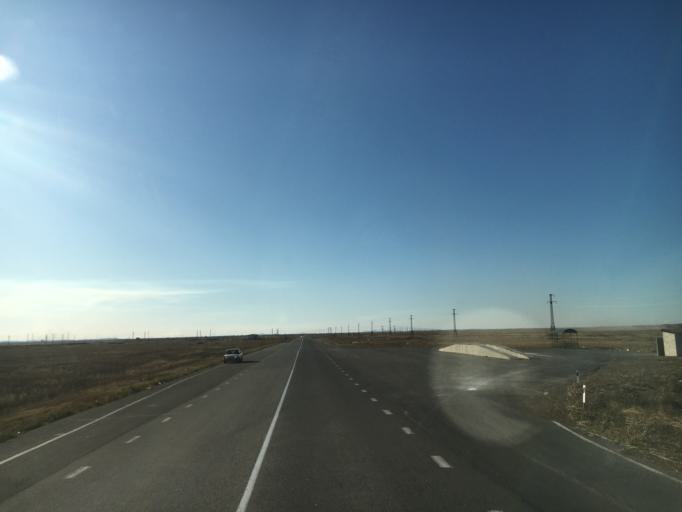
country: KZ
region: Qaraghandy
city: Tokarevka
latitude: 50.0993
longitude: 73.3107
